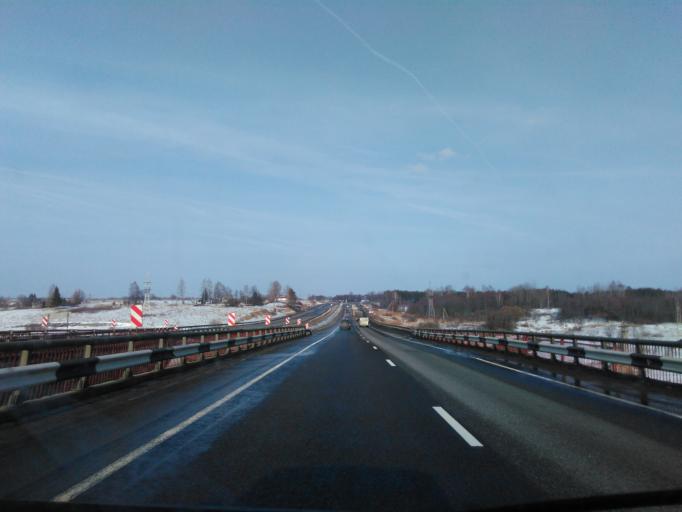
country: RU
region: Smolensk
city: Vyaz'ma
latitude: 55.2056
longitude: 34.1491
